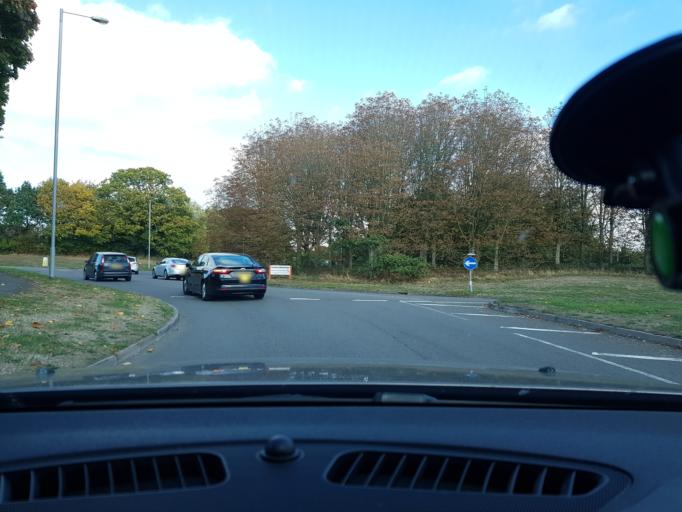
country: GB
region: England
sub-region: Borough of Swindon
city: Chiseldon
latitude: 51.5485
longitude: -1.7374
